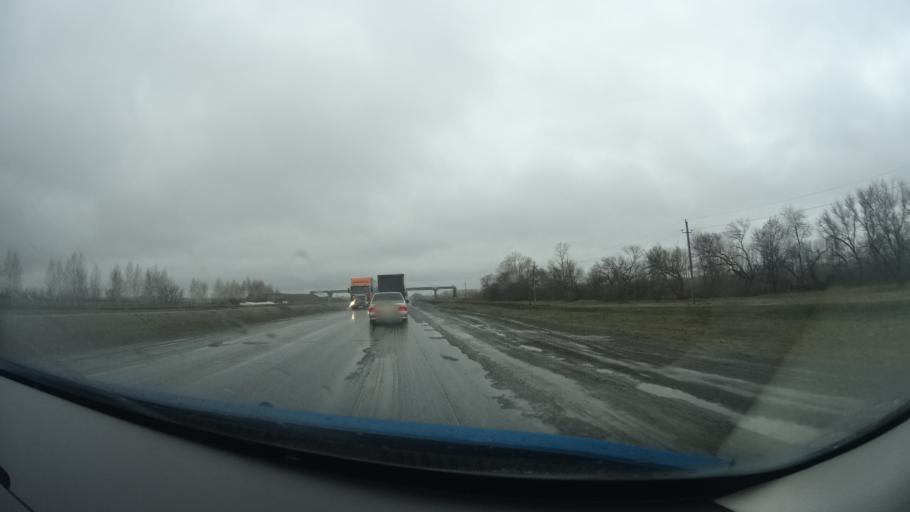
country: RU
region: Bashkortostan
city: Buzdyak
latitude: 54.6506
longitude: 54.6073
